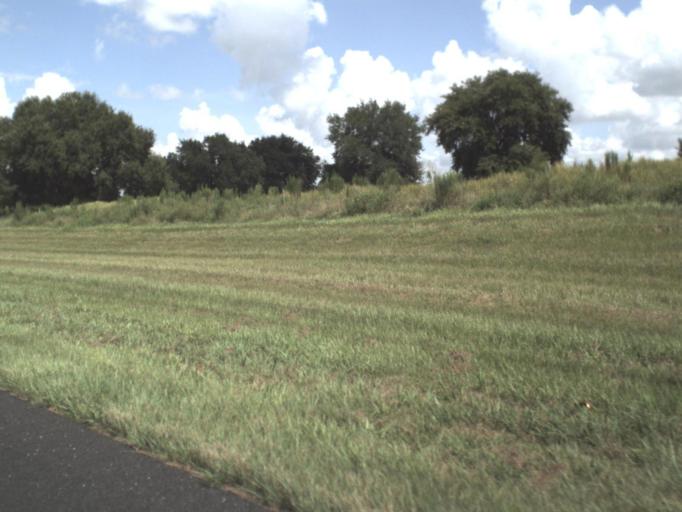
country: US
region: Florida
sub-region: Polk County
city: Fort Meade
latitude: 27.8072
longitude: -81.8193
